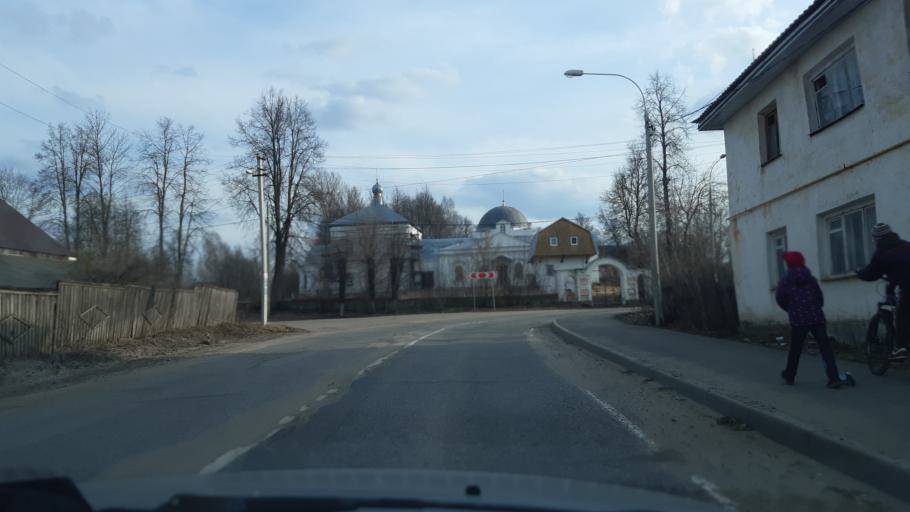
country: RU
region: Vladimir
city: Nikologory
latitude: 56.1418
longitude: 41.9937
